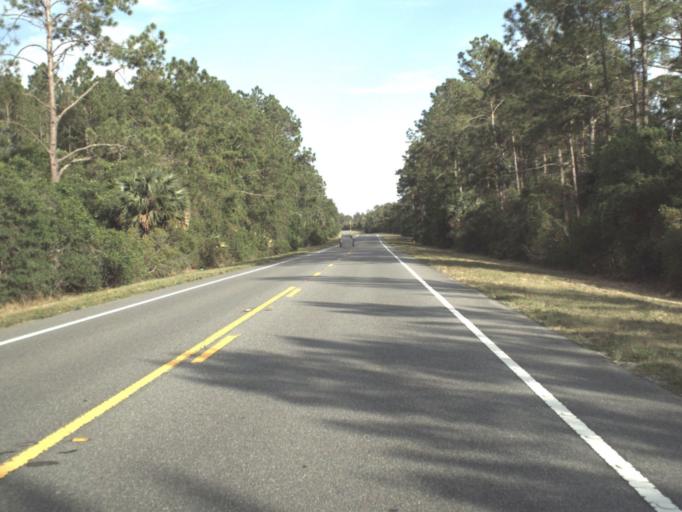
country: US
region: Florida
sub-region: Lake County
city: Astor
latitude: 29.1648
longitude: -81.6083
